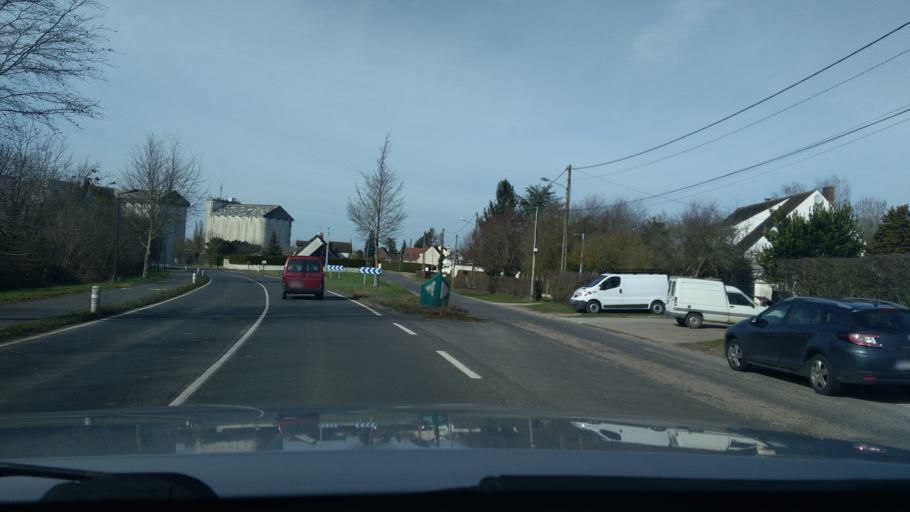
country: FR
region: Ile-de-France
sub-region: Departement de Seine-et-Marne
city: Livry-sur-Seine
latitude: 48.5136
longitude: 2.6765
